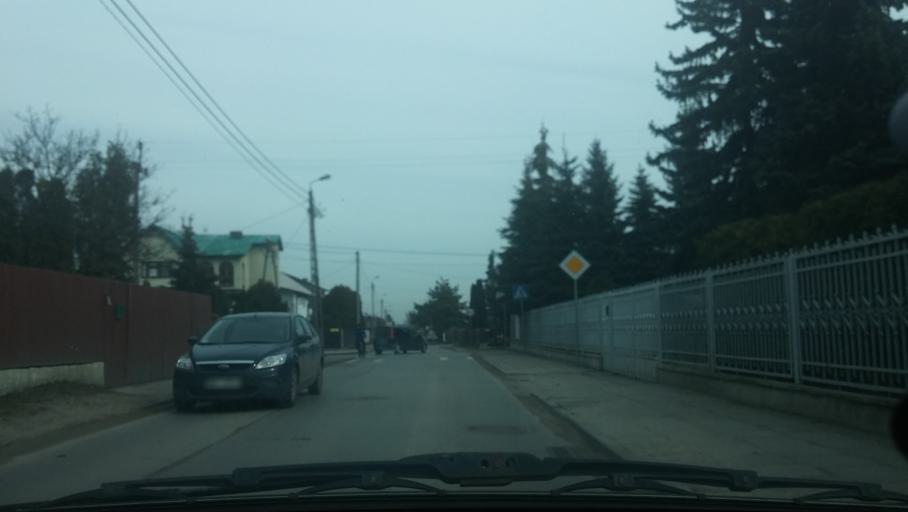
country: PL
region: Masovian Voivodeship
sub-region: Powiat wolominski
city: Marki
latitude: 52.3138
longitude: 21.1113
